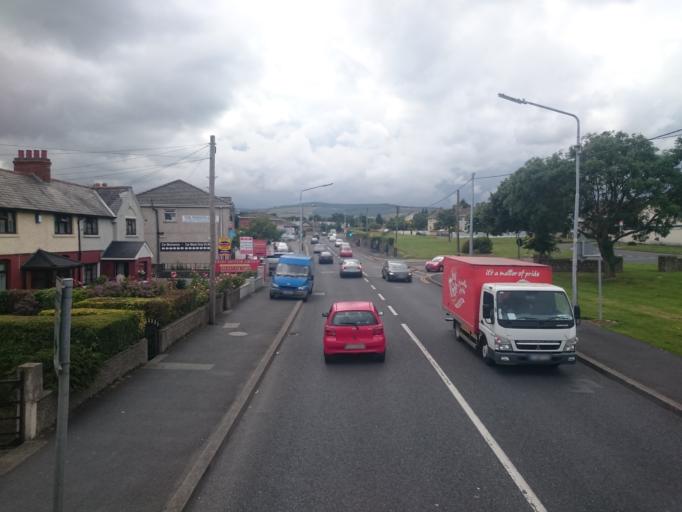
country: IE
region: Leinster
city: Oldbawn
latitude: 53.2854
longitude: -6.3612
